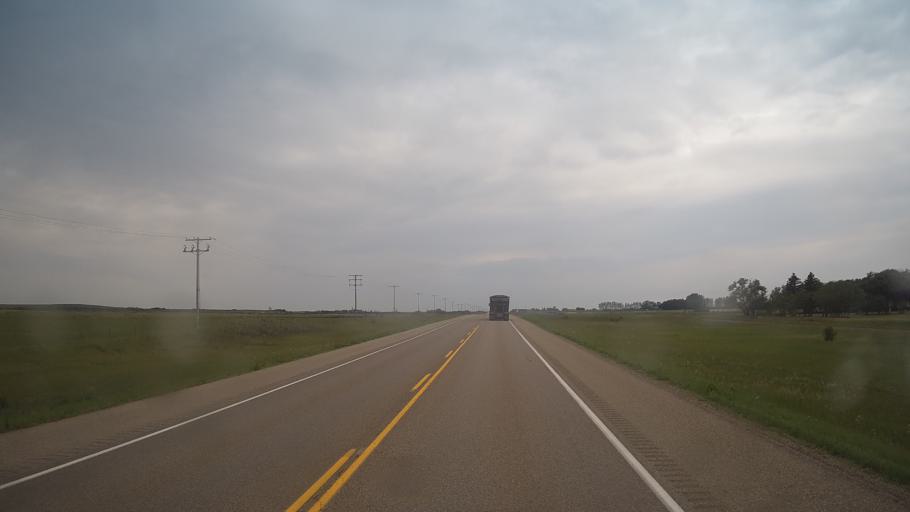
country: CA
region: Saskatchewan
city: Langham
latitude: 52.1289
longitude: -107.1667
